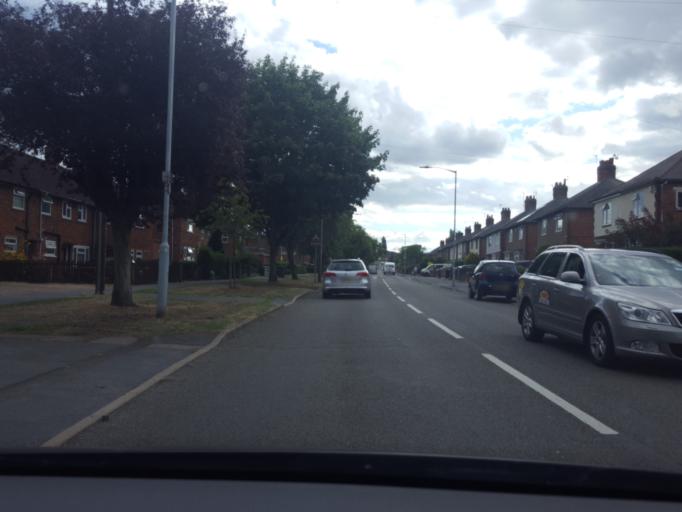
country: GB
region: England
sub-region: Leicestershire
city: Loughborough
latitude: 52.7560
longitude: -1.2102
